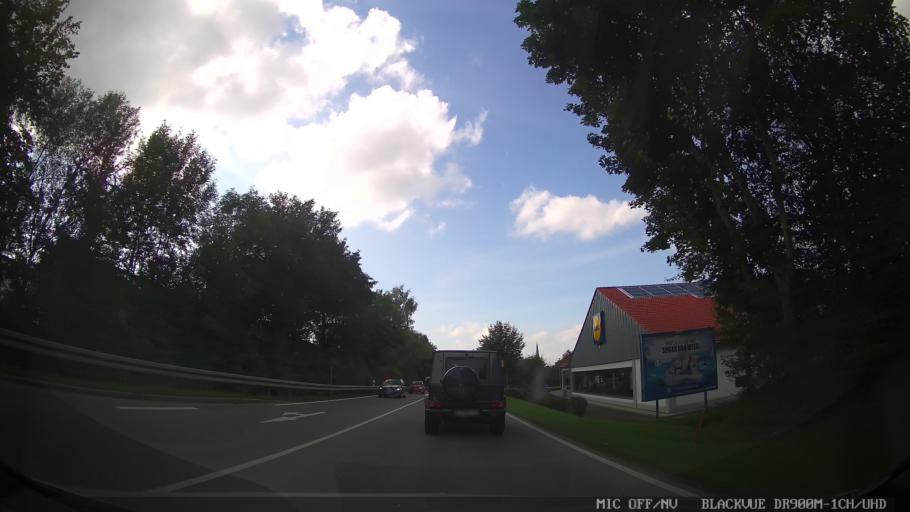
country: DE
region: Baden-Wuerttemberg
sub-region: Freiburg Region
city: Spaichingen
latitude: 48.0694
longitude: 8.7483
